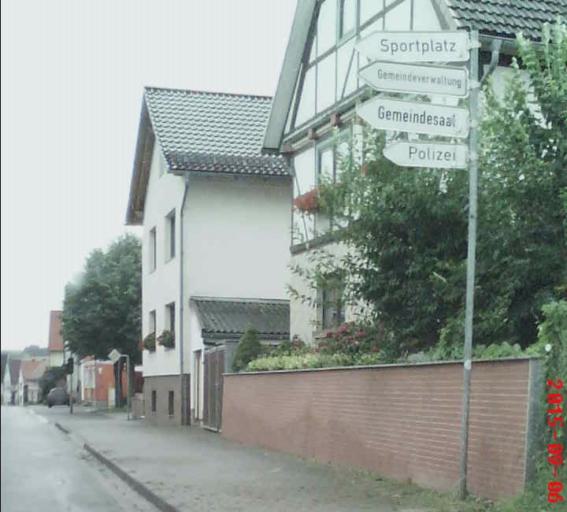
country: DE
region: Thuringia
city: Weissenborn-Luderode
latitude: 51.5323
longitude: 10.4189
